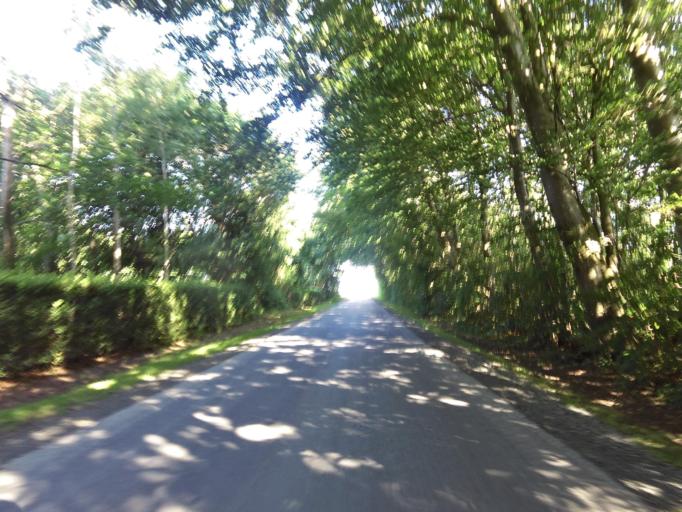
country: DK
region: South Denmark
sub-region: Vejen Kommune
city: Rodding
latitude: 55.3278
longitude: 9.1732
